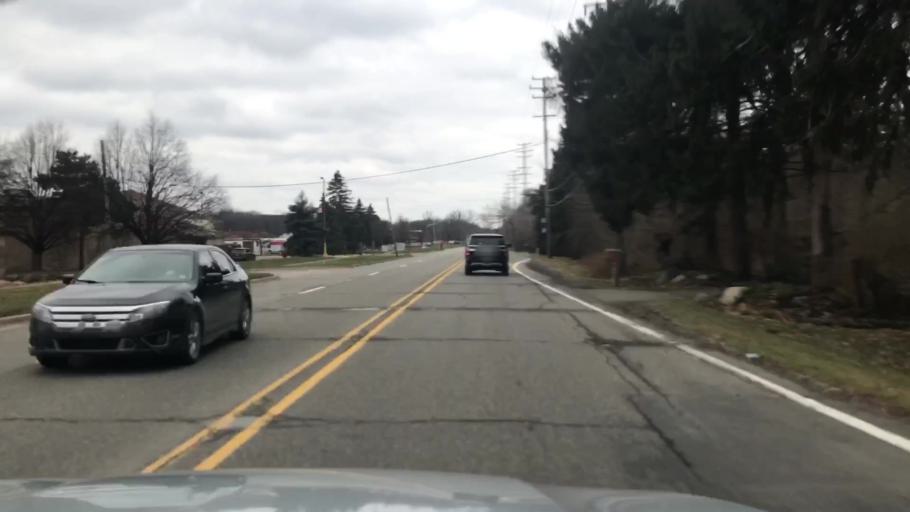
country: US
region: Michigan
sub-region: Wayne County
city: Northville
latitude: 42.4490
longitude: -83.4740
